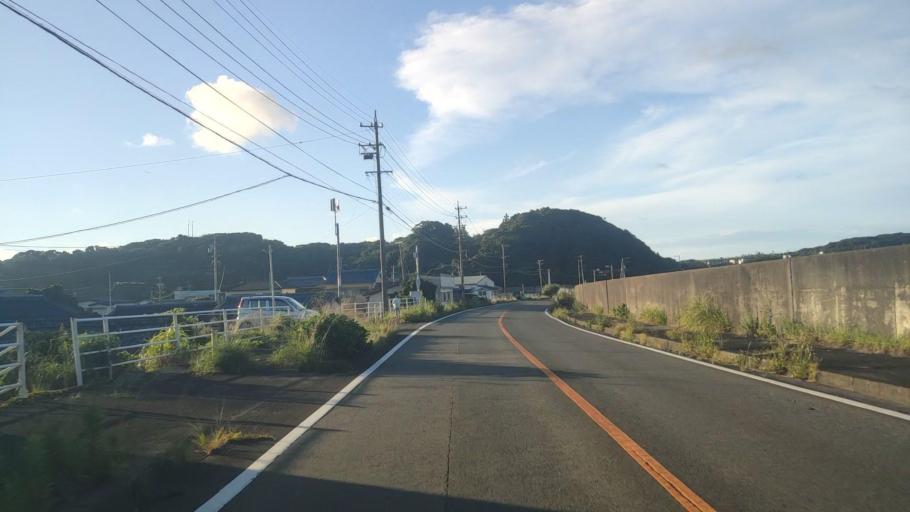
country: JP
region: Mie
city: Toba
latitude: 34.2705
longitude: 136.8683
